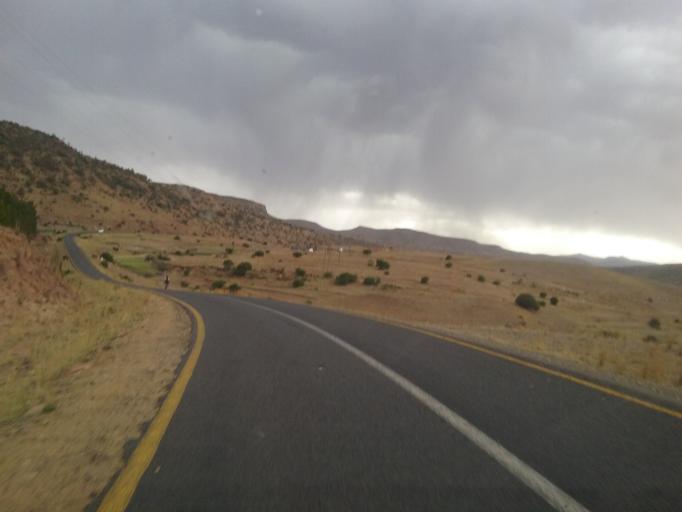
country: LS
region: Quthing
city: Quthing
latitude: -30.2852
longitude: 27.7947
